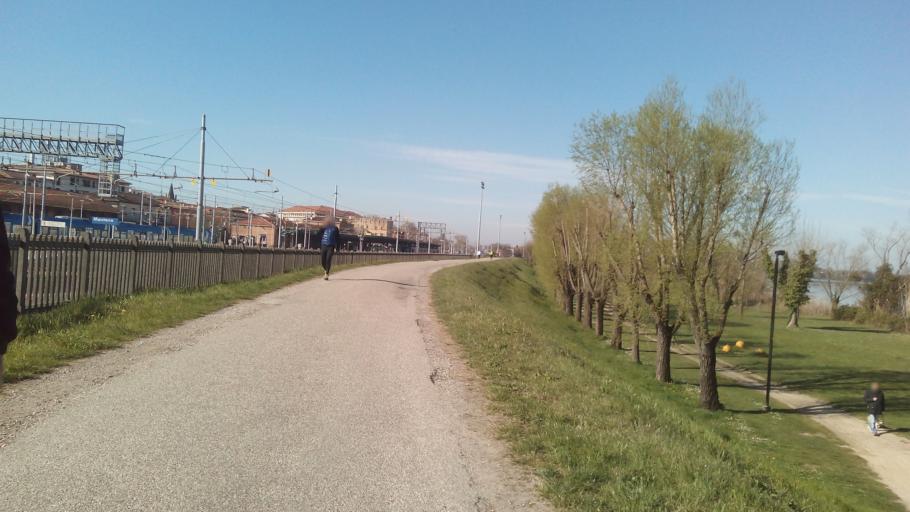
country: IT
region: Lombardy
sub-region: Provincia di Mantova
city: Mantova
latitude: 45.1606
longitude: 10.7859
